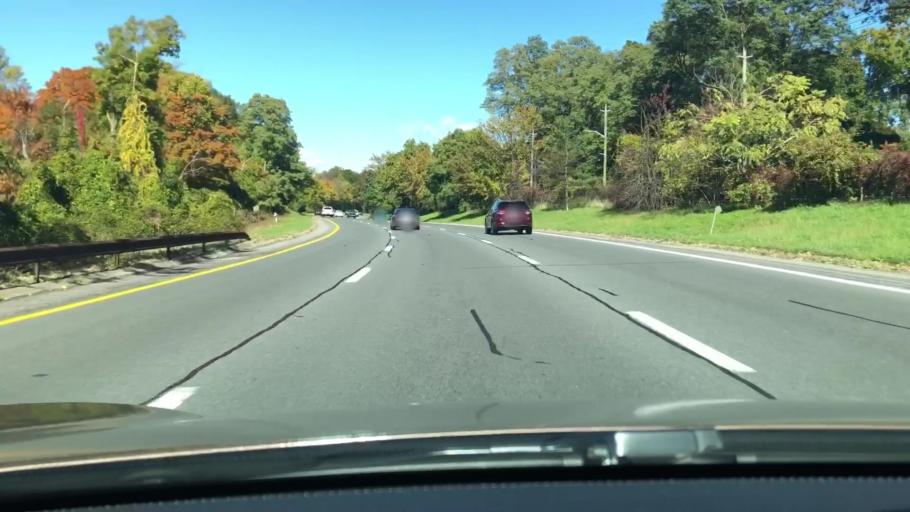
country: US
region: New York
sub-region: Westchester County
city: Tuckahoe
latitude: 40.9654
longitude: -73.8486
